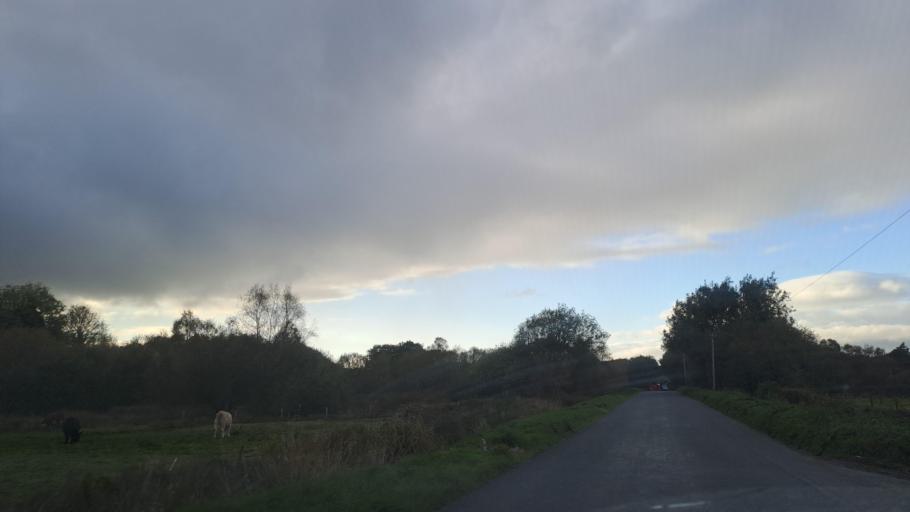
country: IE
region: Ulster
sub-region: County Monaghan
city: Castleblayney
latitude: 54.0372
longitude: -6.8211
